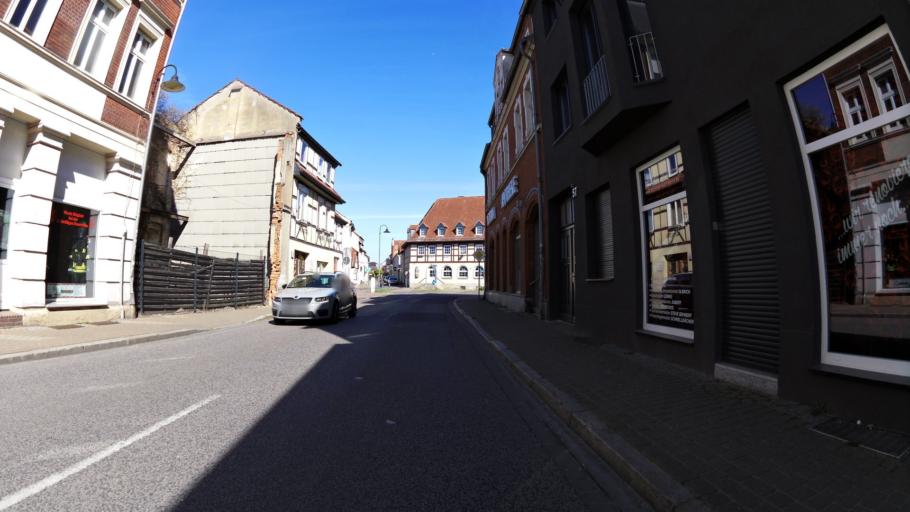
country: DE
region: Saxony-Anhalt
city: Bismark
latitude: 52.6616
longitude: 11.5566
